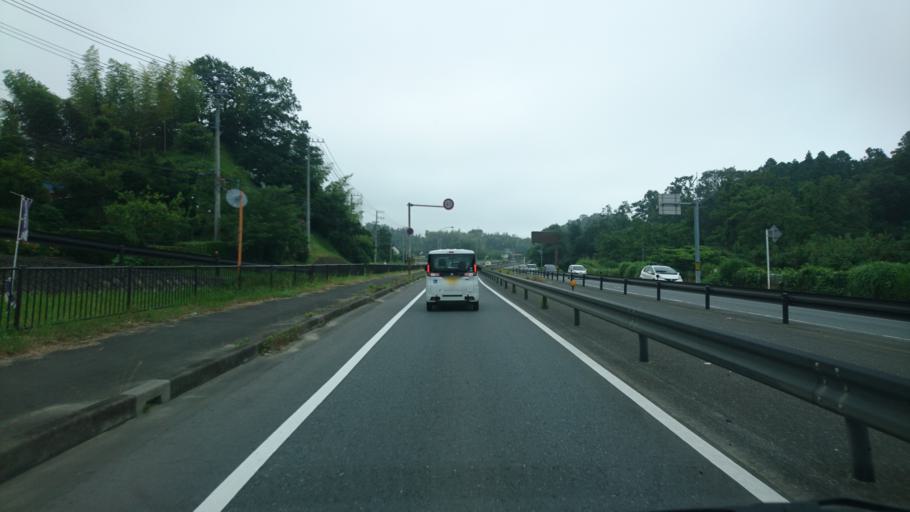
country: JP
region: Chiba
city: Kimitsu
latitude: 35.2505
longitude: 139.8862
